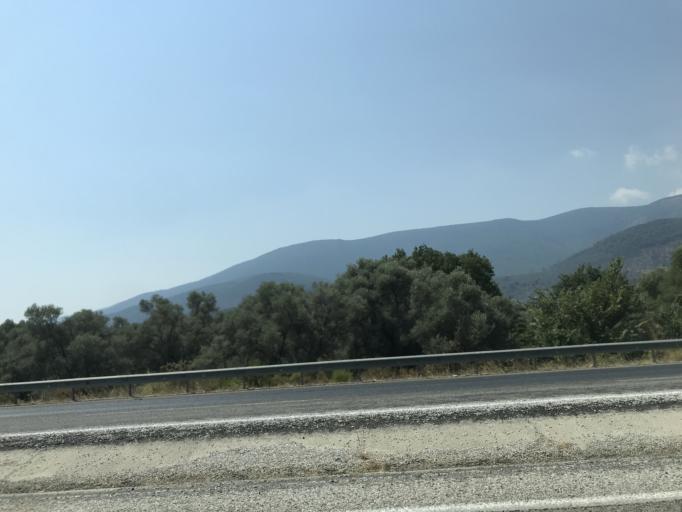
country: TR
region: Mugla
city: Selimiye
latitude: 37.4186
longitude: 27.6120
